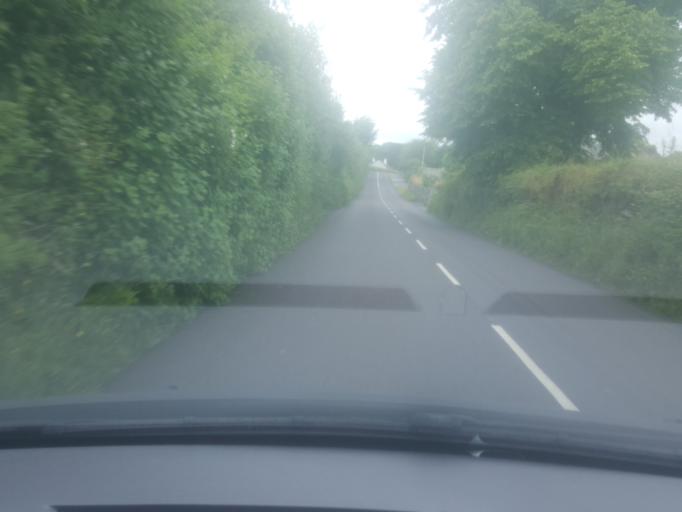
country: IE
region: Munster
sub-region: Ciarrai
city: Cill Airne
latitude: 52.0722
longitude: -9.5072
